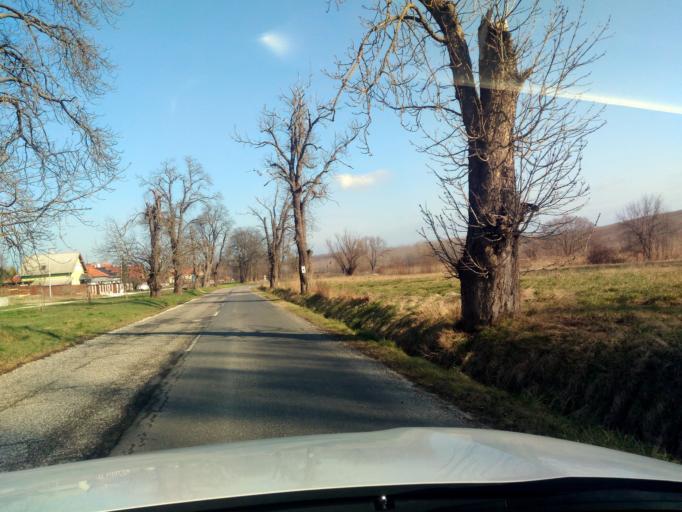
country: HU
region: Fejer
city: Etyek
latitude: 47.4581
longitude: 18.7262
